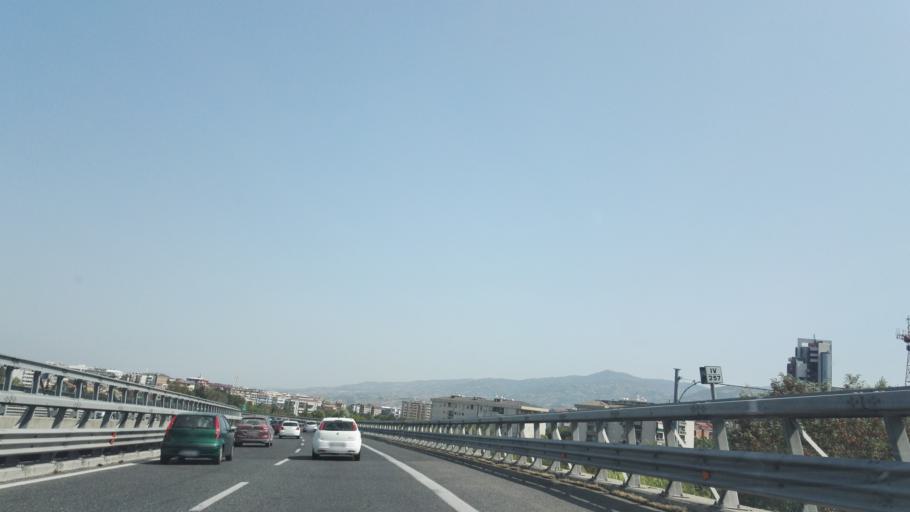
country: IT
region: Calabria
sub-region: Provincia di Cosenza
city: Cosenza
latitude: 39.3148
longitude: 16.2411
